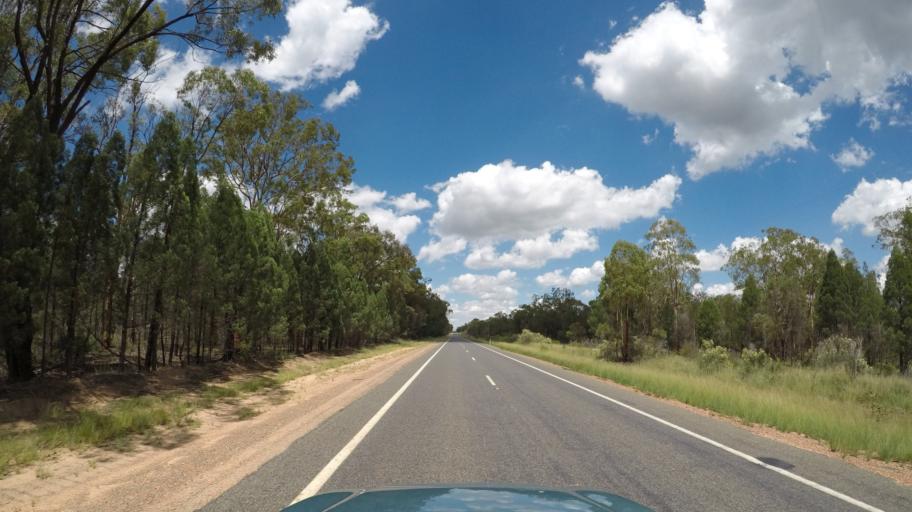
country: AU
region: Queensland
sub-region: Goondiwindi
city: Goondiwindi
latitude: -27.9931
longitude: 150.9546
